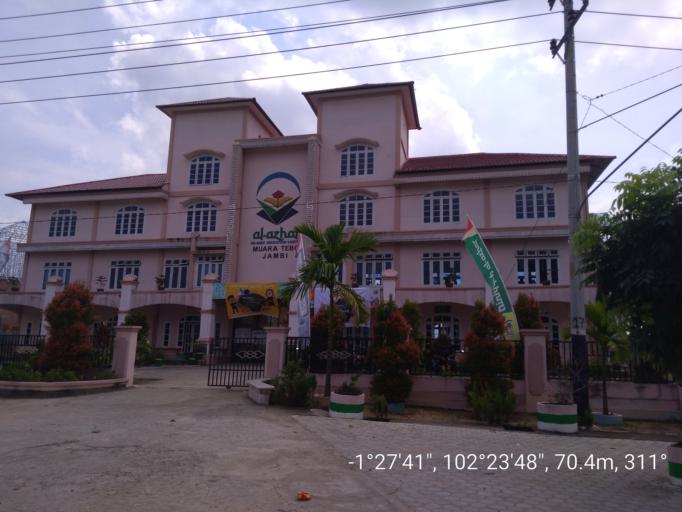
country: ID
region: Jambi
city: Muara Tebo
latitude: -1.4615
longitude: 102.3969
